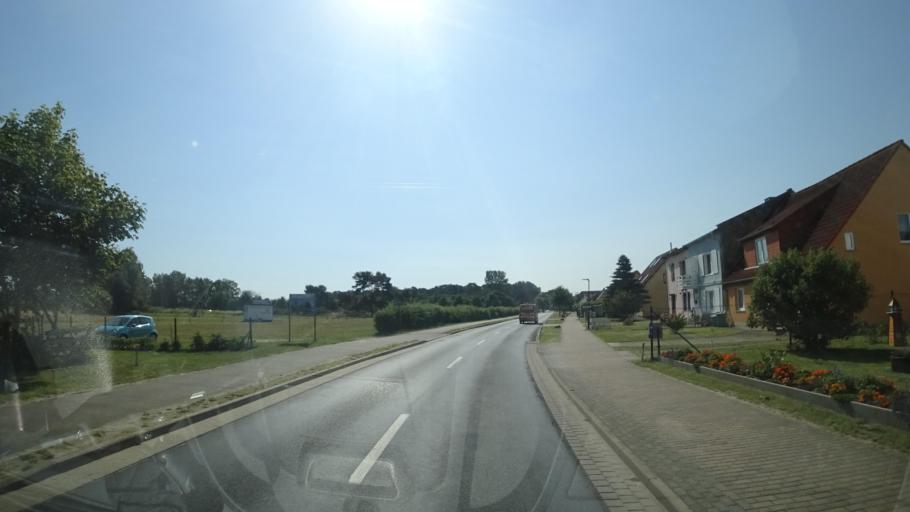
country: DE
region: Mecklenburg-Vorpommern
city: Kroslin
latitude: 54.1354
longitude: 13.7300
